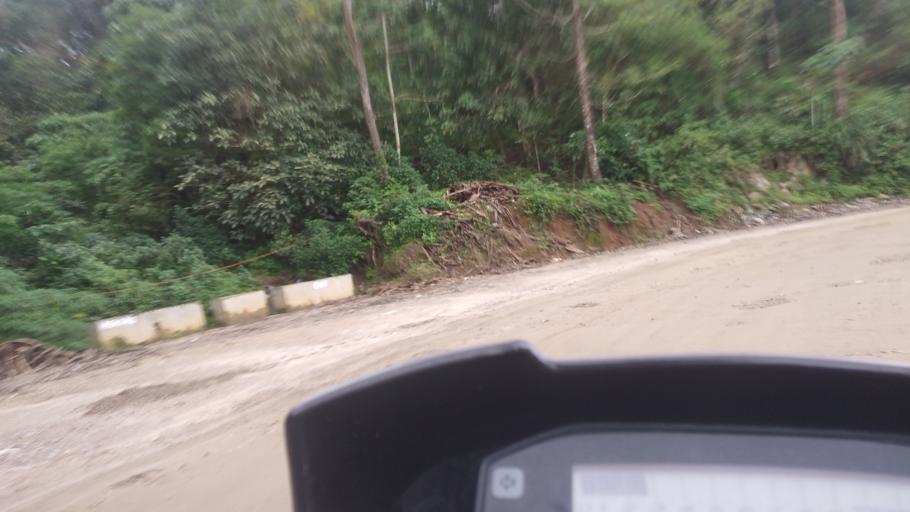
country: IN
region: Kerala
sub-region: Idukki
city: Munnar
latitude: 10.0355
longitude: 77.1413
